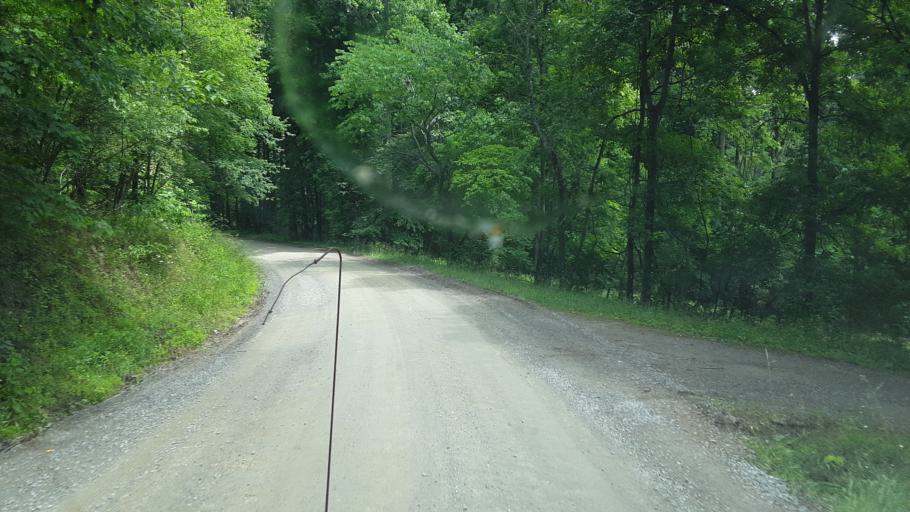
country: US
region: Virginia
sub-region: Pittsylvania County
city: Chatham
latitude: 36.8441
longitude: -79.4306
